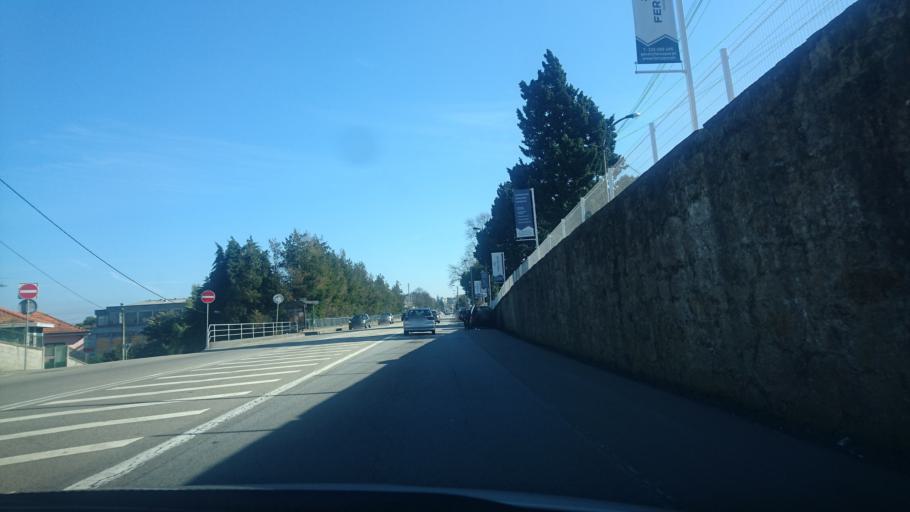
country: PT
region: Porto
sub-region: Vila Nova de Gaia
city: Vilar de Andorinho
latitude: 41.1194
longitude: -8.5985
